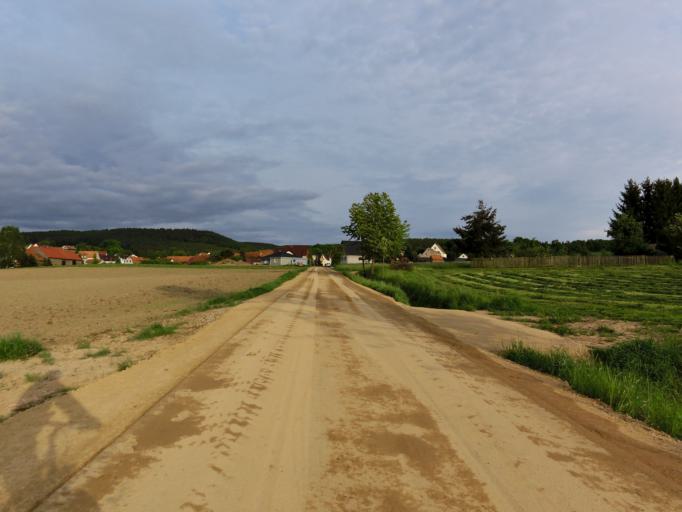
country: DE
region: Thuringia
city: Frauensee
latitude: 50.9094
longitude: 10.0952
